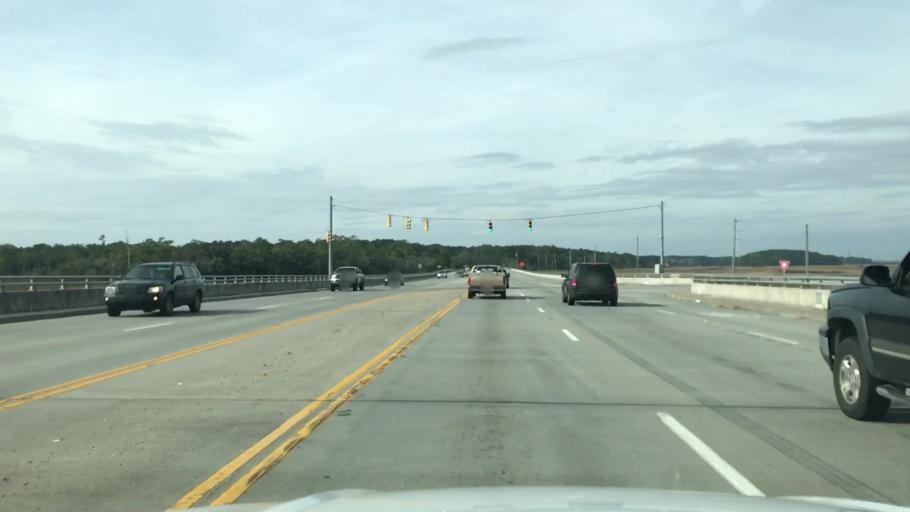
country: US
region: South Carolina
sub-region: Charleston County
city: Shell Point
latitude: 32.7515
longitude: -80.0221
